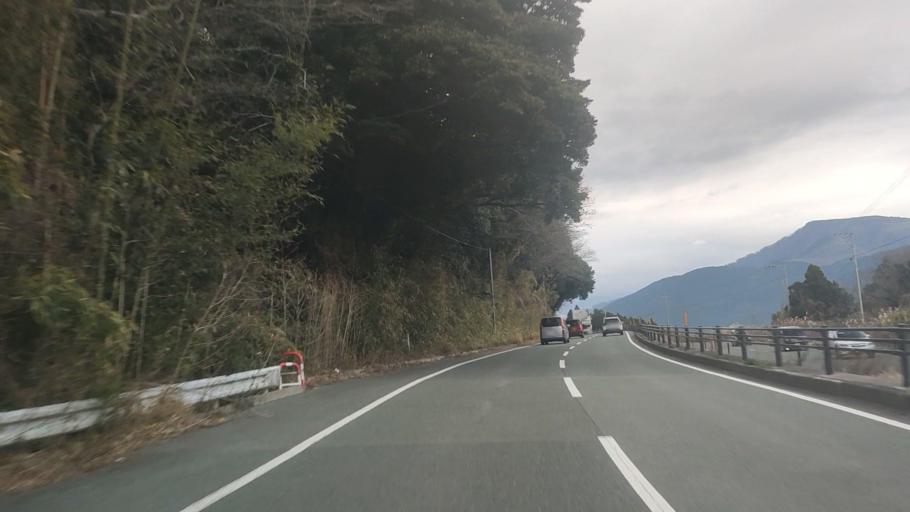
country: JP
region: Kumamoto
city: Ozu
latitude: 32.8762
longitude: 130.9355
